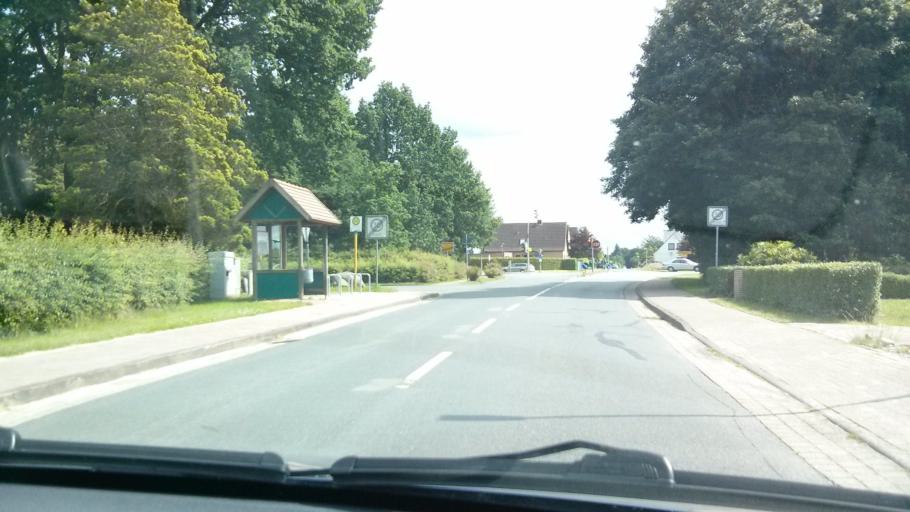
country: DE
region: Lower Saxony
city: Schiffdorf
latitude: 53.5273
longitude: 8.6575
